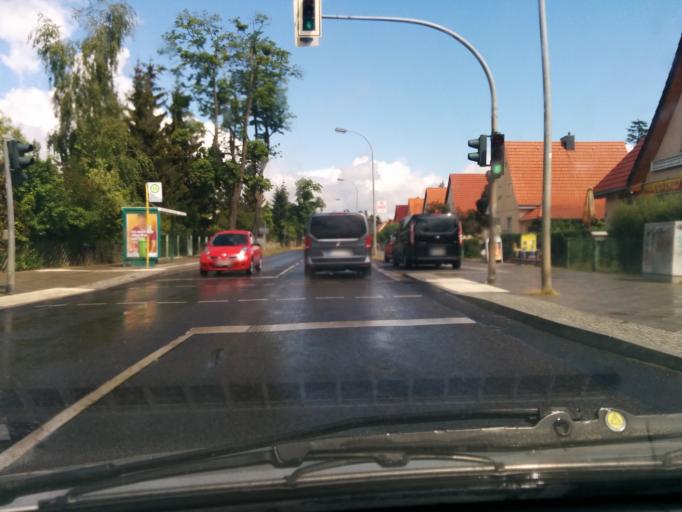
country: DE
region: Brandenburg
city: Falkensee
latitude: 52.5708
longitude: 13.1047
